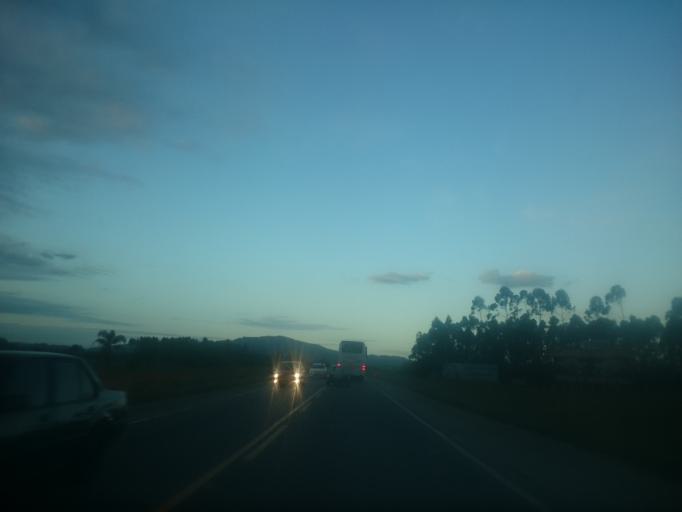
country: BR
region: Santa Catarina
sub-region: Gaspar
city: Gaspar
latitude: -26.8779
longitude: -48.8287
